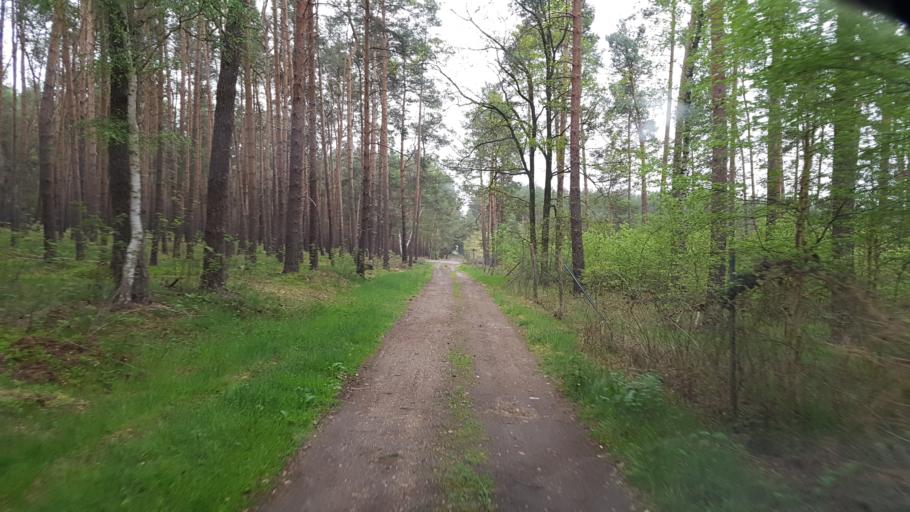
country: DE
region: Brandenburg
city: Schonewalde
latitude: 51.7094
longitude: 13.5606
